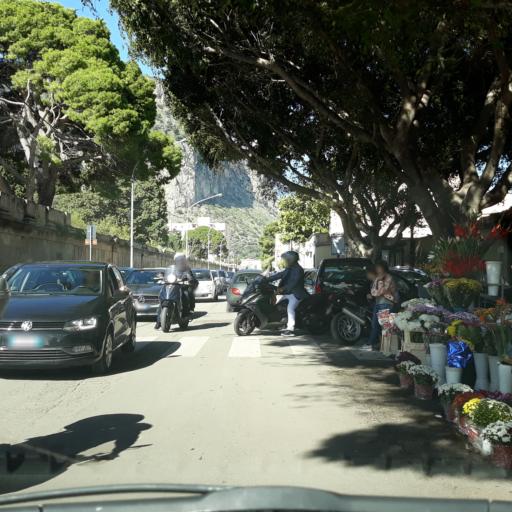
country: IT
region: Sicily
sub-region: Palermo
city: Palermo
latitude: 38.1618
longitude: 13.3707
